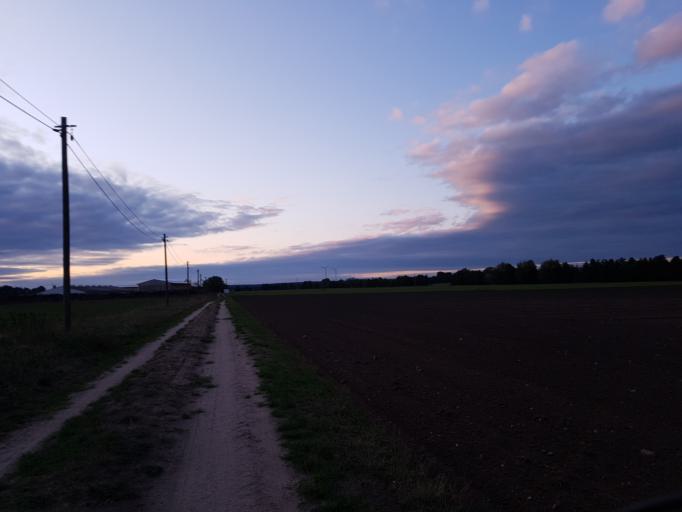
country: DE
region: Brandenburg
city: Schilda
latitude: 51.6094
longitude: 13.3610
